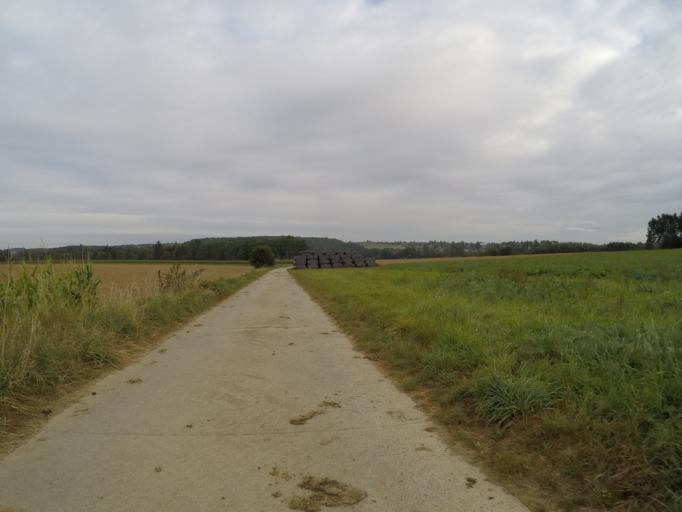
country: BE
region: Wallonia
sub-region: Province de Namur
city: Ciney
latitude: 50.3211
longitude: 5.0541
